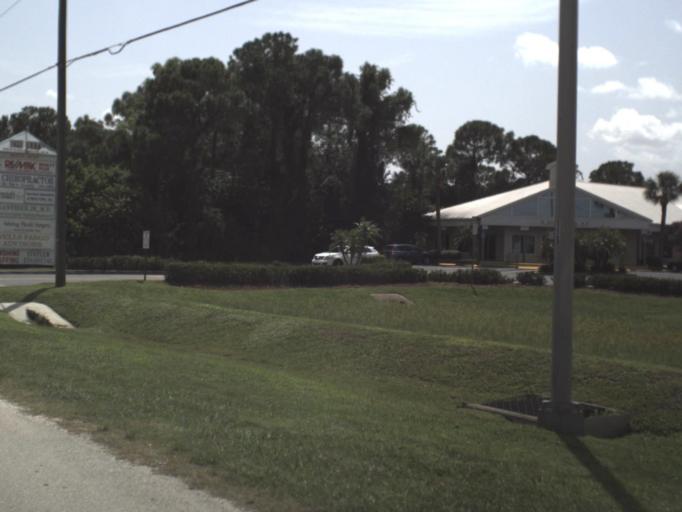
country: US
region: Florida
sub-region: Highlands County
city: Sebring
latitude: 27.4756
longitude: -81.4726
